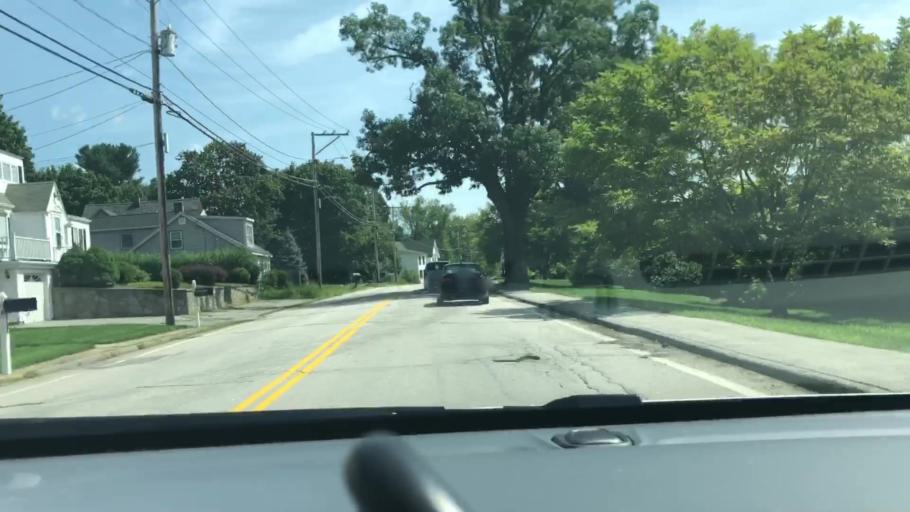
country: US
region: New Hampshire
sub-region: Hillsborough County
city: Pinardville
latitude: 42.9870
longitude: -71.4995
